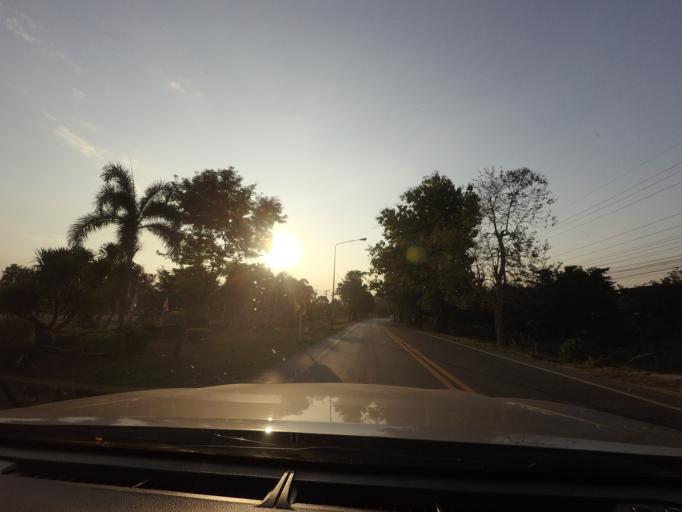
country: TH
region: Phitsanulok
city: Noen Maprang
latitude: 16.6893
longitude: 100.5395
